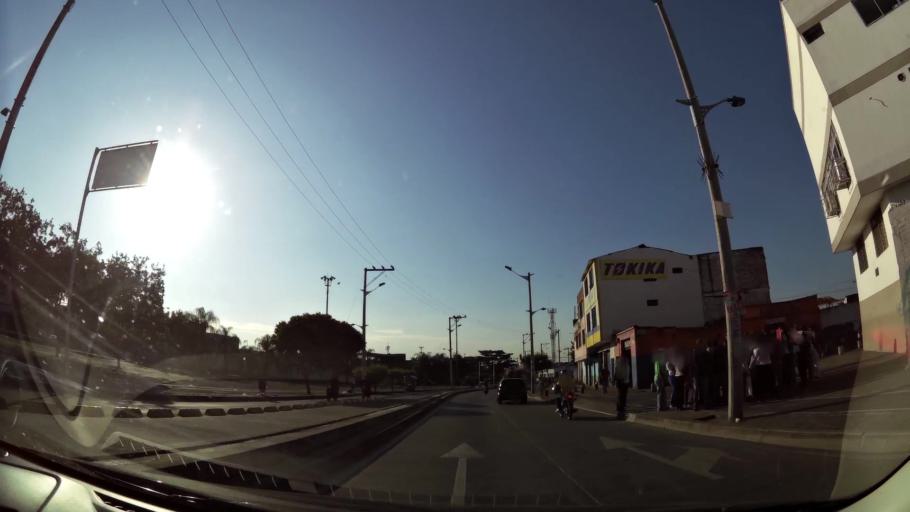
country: CO
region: Valle del Cauca
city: Cali
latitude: 3.4421
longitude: -76.5251
